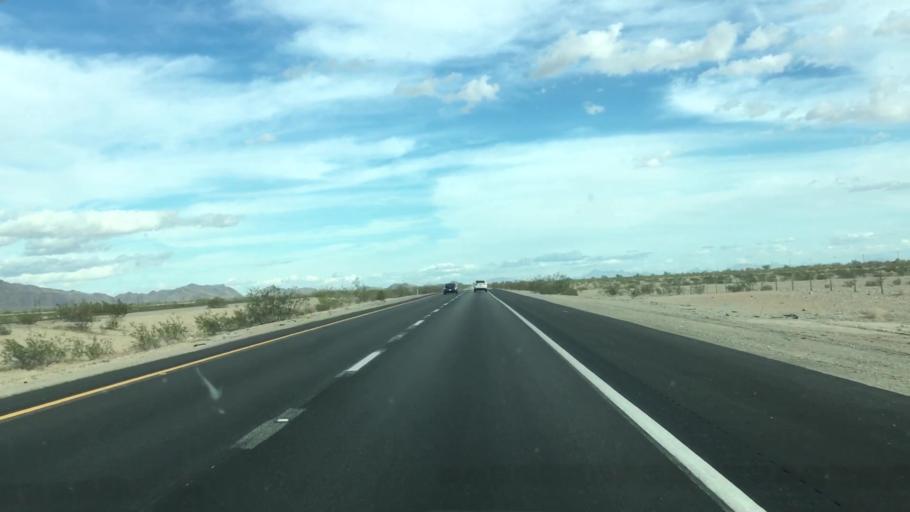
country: US
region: California
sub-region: Riverside County
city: Mesa Verde
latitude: 33.6089
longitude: -114.8626
